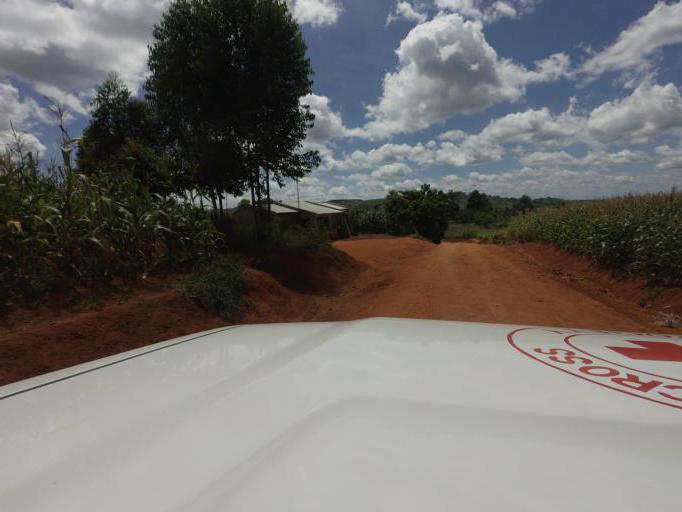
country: MW
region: Southern Region
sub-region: Thyolo District
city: Thyolo
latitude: -16.0299
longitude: 35.0486
